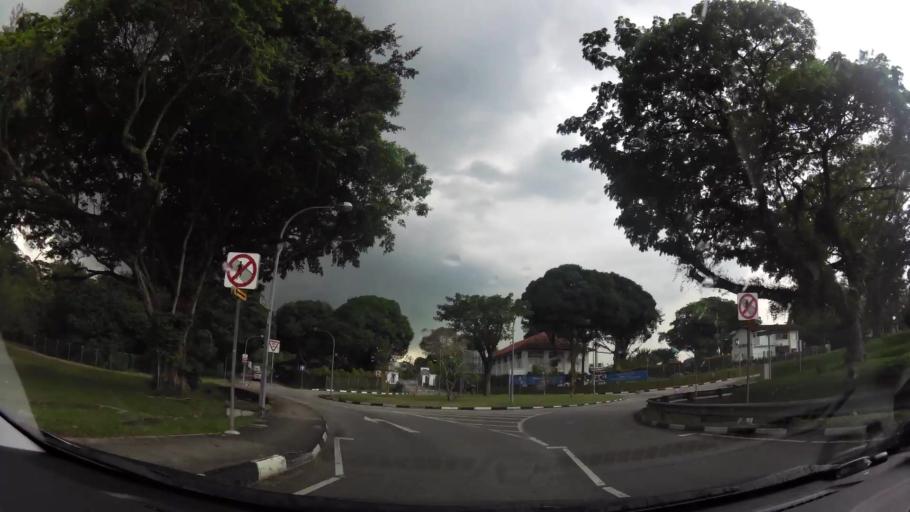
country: MY
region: Johor
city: Kampung Pasir Gudang Baru
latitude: 1.4035
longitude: 103.8716
